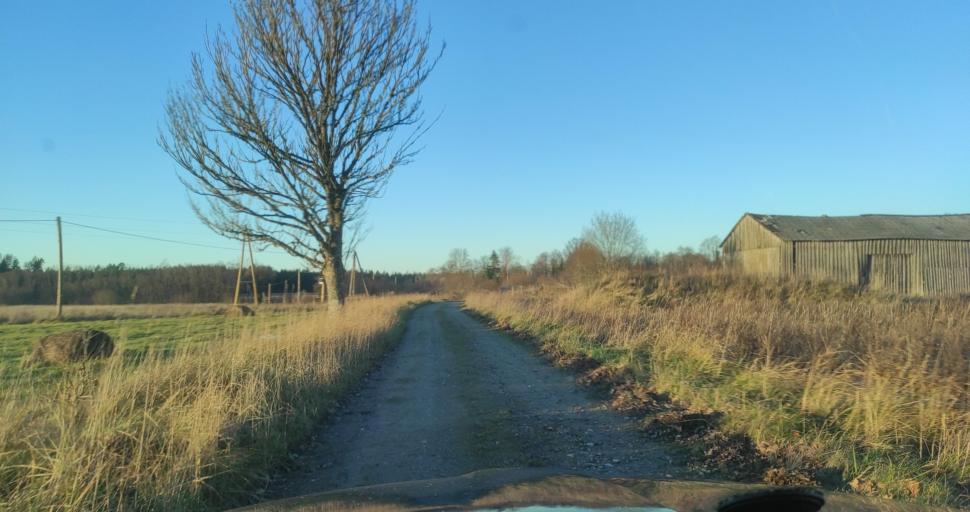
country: LV
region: Dundaga
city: Dundaga
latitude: 57.3901
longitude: 22.0898
